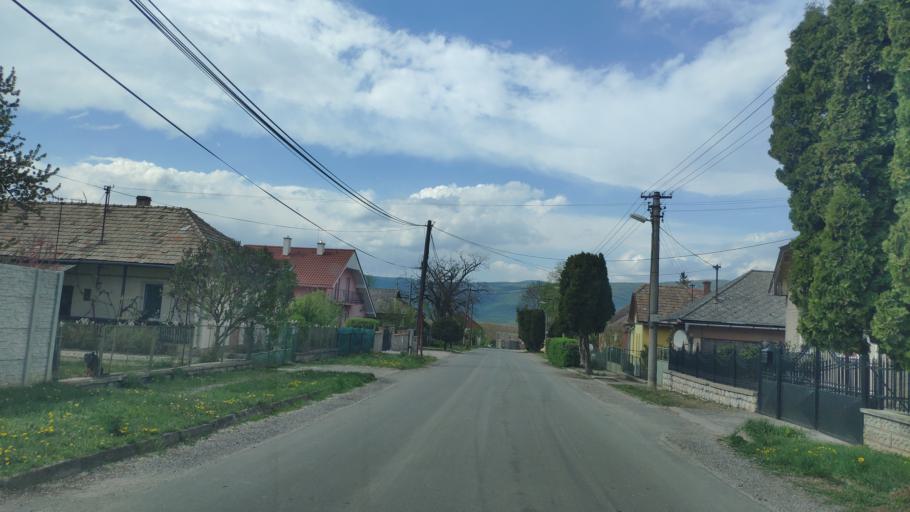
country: SK
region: Kosicky
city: Moldava nad Bodvou
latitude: 48.5840
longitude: 20.9213
